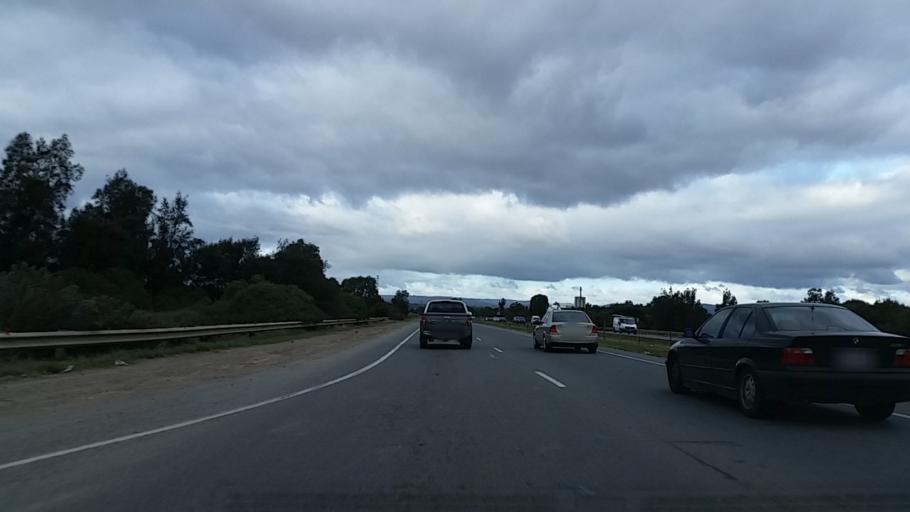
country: AU
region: South Australia
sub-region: Port Adelaide Enfield
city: Blair Athol
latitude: -34.8327
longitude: 138.5748
